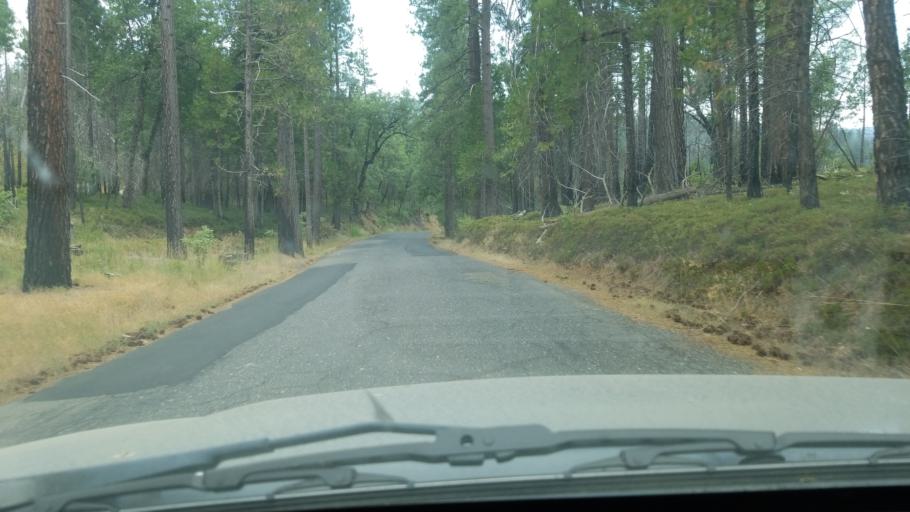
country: US
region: California
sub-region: Mariposa County
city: Midpines
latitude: 37.8225
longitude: -119.8646
